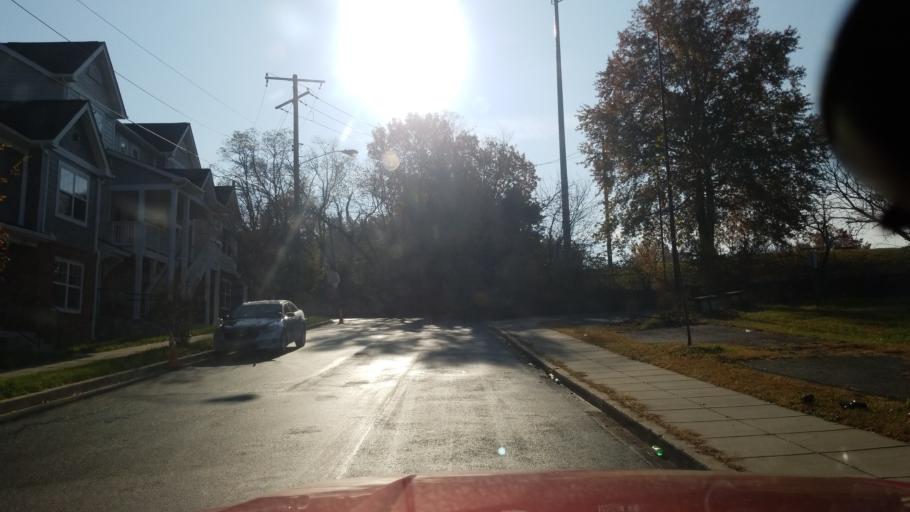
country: US
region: Maryland
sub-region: Prince George's County
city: Capitol Heights
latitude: 38.8853
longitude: -76.9328
